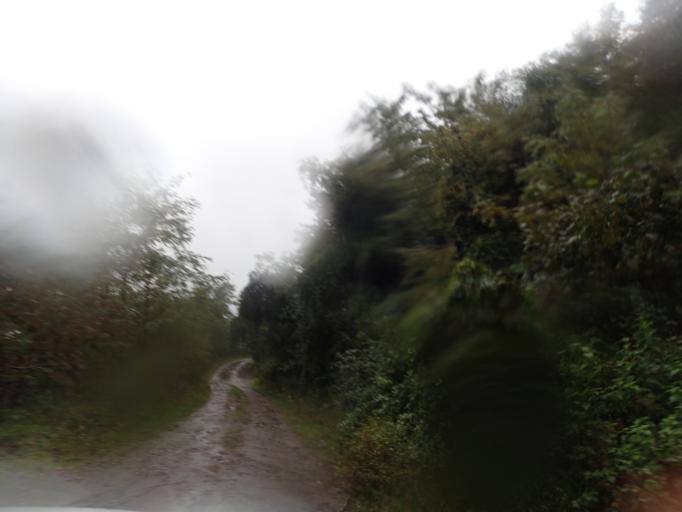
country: TR
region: Ordu
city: Persembe
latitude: 41.0371
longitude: 37.7337
